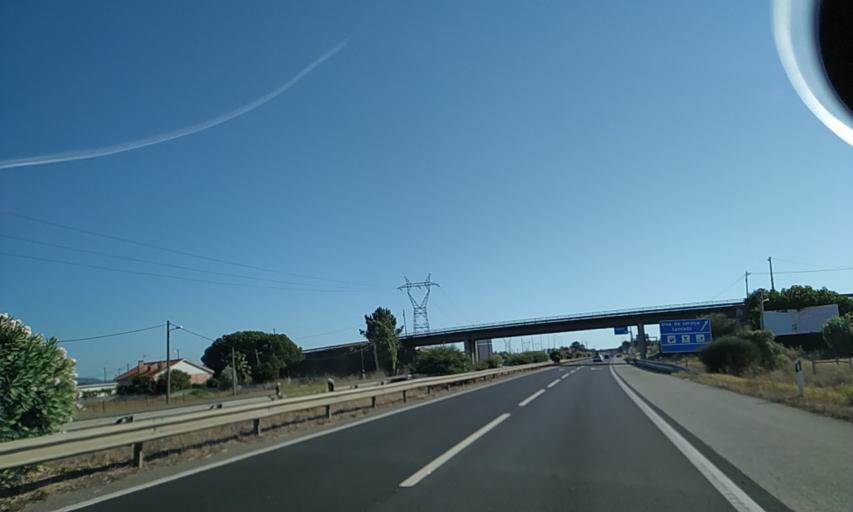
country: PT
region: Setubal
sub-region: Moita
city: Moita
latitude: 38.6674
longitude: -8.9542
